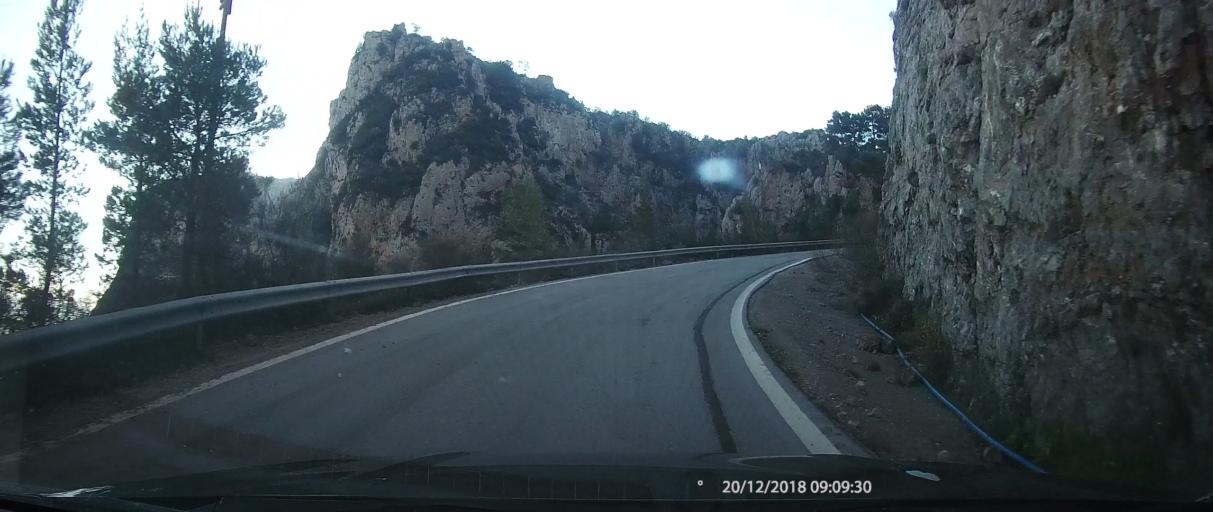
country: GR
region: Peloponnese
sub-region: Nomos Lakonias
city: Sykea
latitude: 36.9169
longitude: 23.0034
